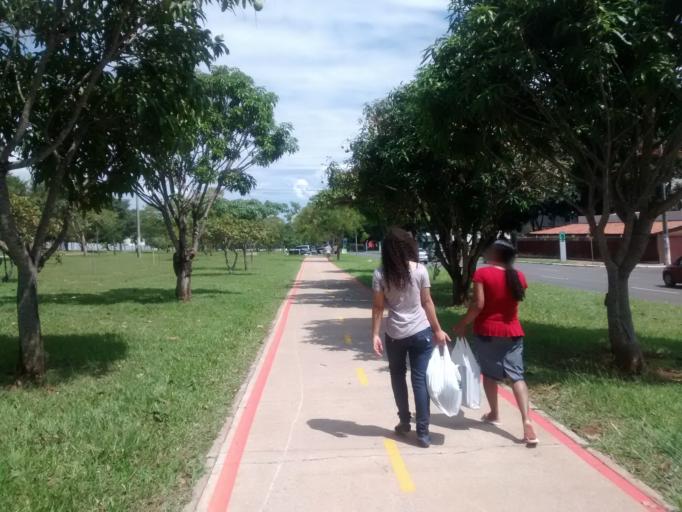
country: BR
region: Federal District
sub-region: Brasilia
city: Brasilia
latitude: -15.7626
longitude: -47.8945
